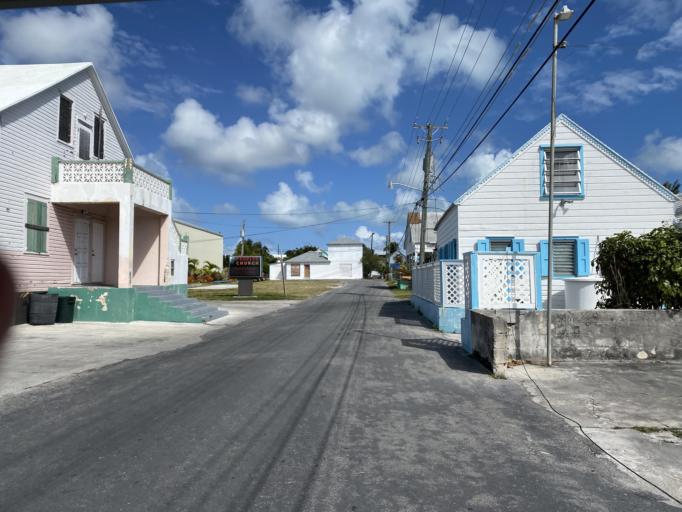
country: BS
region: Spanish Wells
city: Spanish Wells
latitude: 25.5437
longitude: -76.7459
